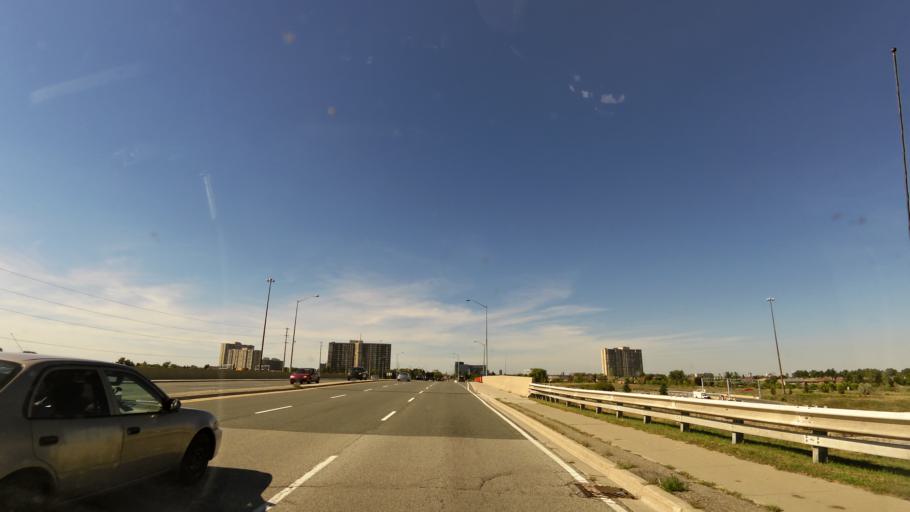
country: CA
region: Ontario
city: Brampton
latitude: 43.6531
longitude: -79.7157
